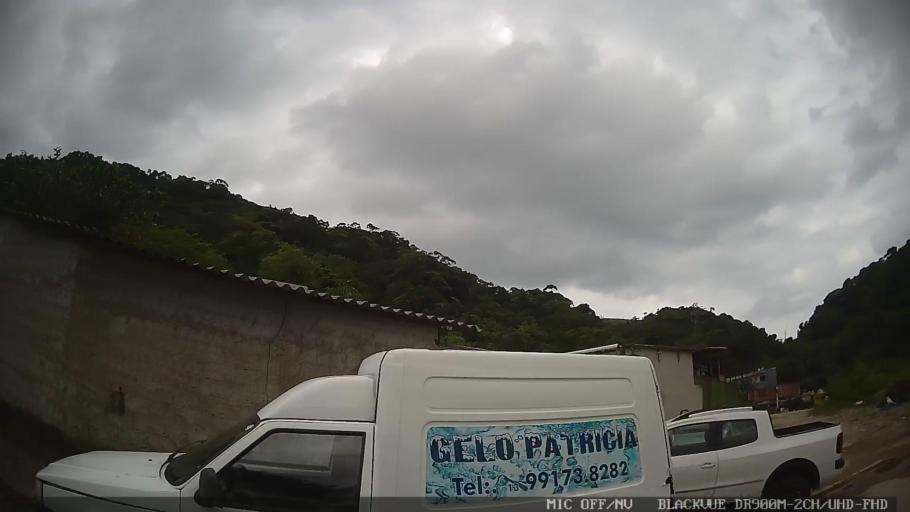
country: BR
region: Sao Paulo
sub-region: Guaruja
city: Guaruja
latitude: -23.9968
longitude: -46.2699
